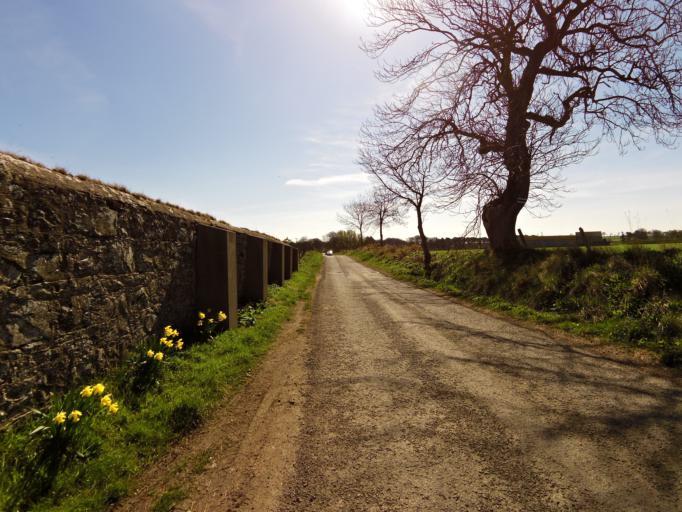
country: GB
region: Scotland
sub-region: Angus
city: Montrose
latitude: 56.6935
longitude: -2.4596
